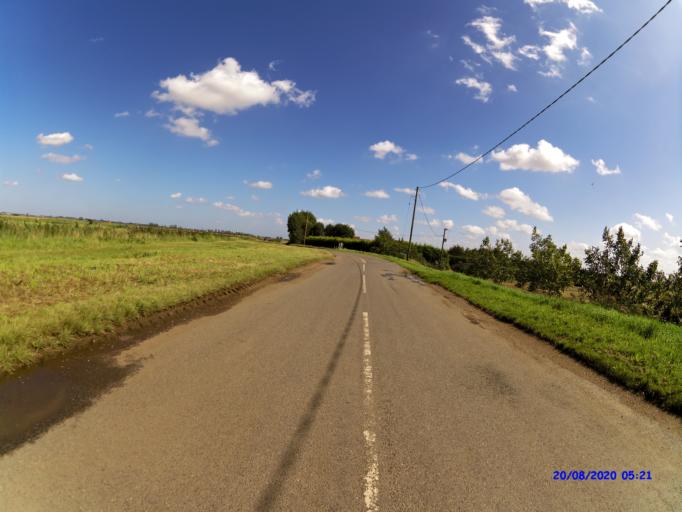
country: GB
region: England
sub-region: Cambridgeshire
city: Whittlesey
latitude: 52.5285
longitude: -0.1027
